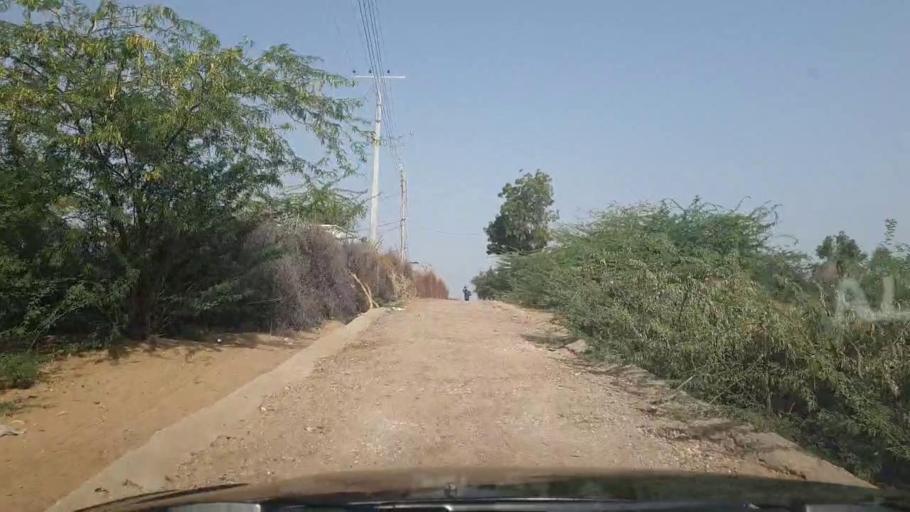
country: PK
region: Sindh
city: Islamkot
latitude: 25.0078
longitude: 70.2104
